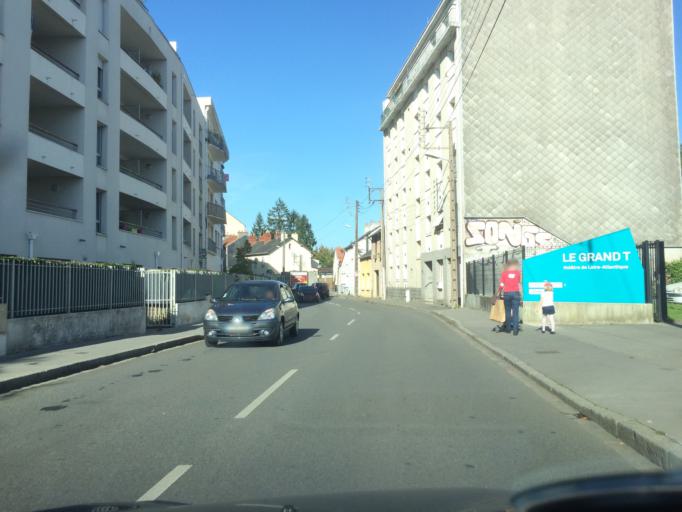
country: FR
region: Pays de la Loire
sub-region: Departement de la Loire-Atlantique
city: Nantes
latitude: 47.2312
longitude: -1.5431
